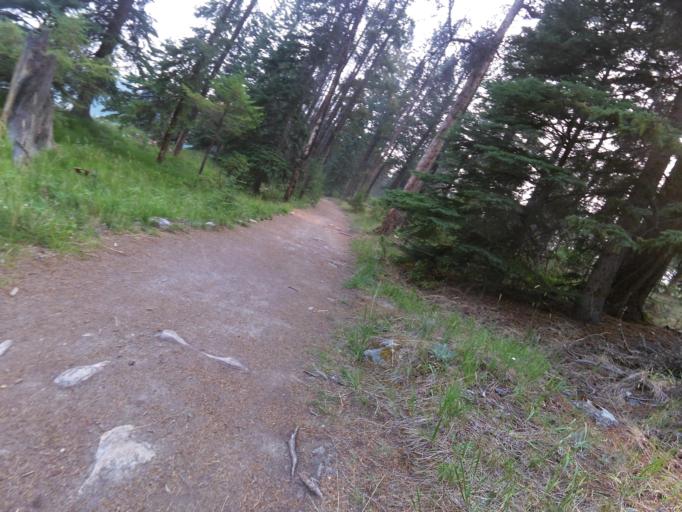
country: CA
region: Alberta
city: Jasper Park Lodge
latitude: 52.8808
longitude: -118.0549
